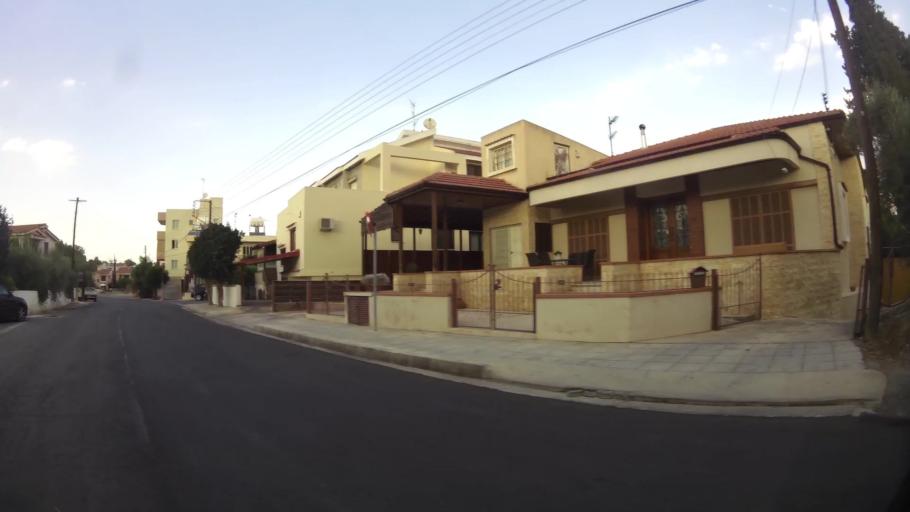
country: CY
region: Lefkosia
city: Tseri
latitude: 35.1189
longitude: 33.3123
